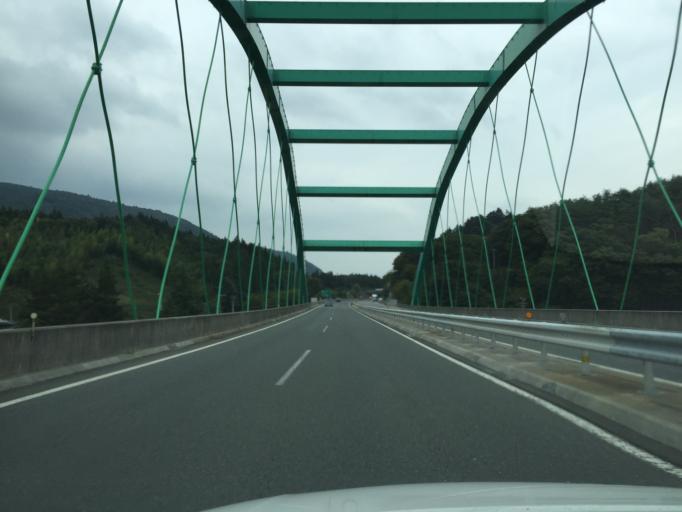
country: JP
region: Fukushima
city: Iwaki
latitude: 37.0968
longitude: 140.7765
